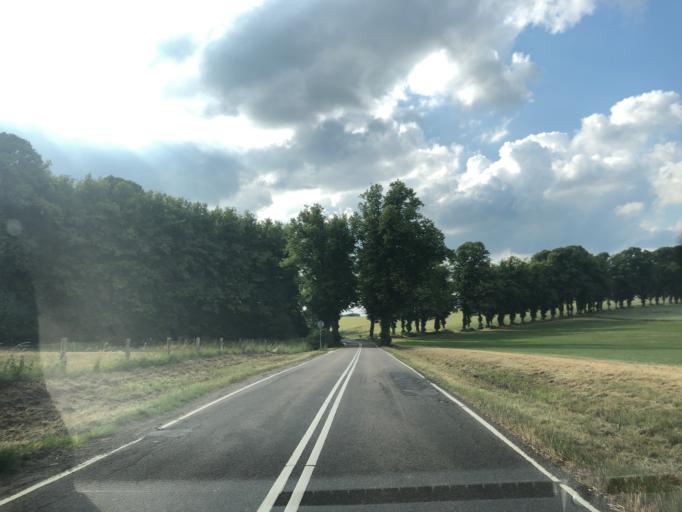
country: DK
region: Zealand
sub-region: Faxe Kommune
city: Ronnede
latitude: 55.3096
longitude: 12.0236
